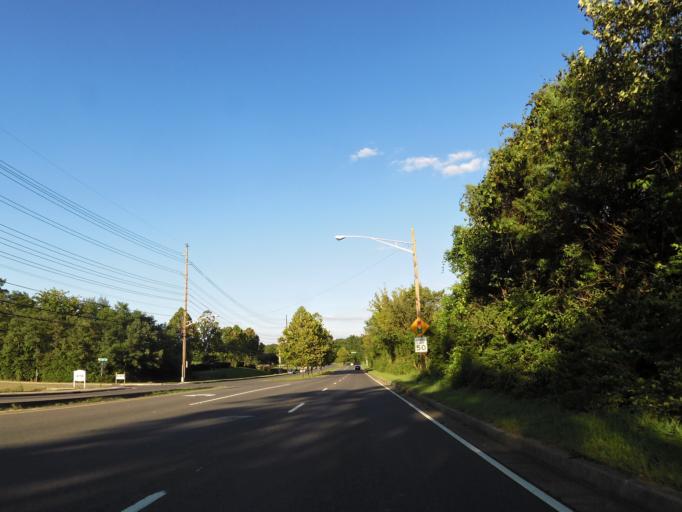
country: US
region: Tennessee
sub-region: Knox County
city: Knoxville
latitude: 35.9451
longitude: -84.0257
